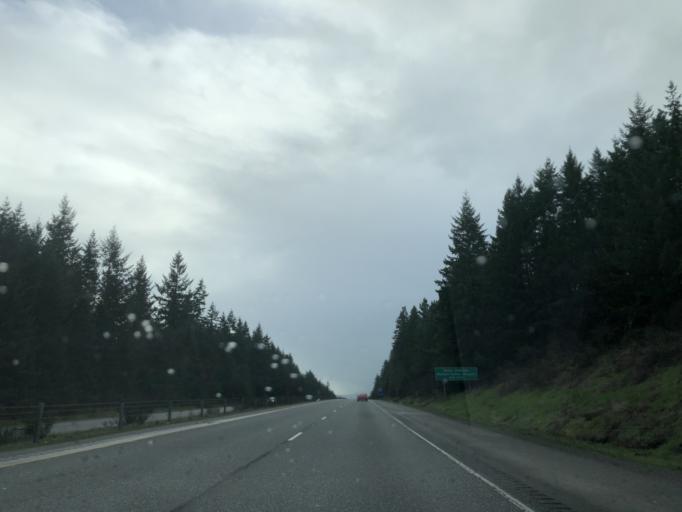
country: US
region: Washington
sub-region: Kitsap County
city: Bangor Trident Base
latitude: 47.7143
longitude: -122.6810
